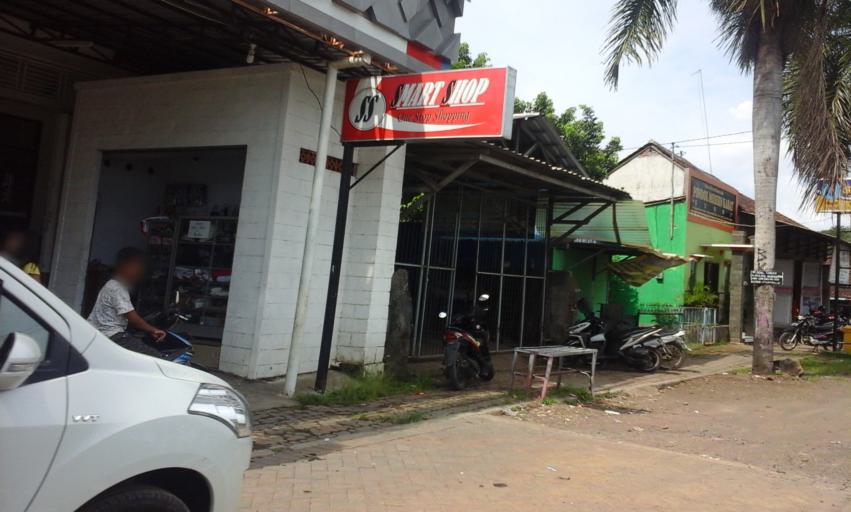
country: ID
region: East Java
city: Kertosari
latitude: -8.2625
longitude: 114.3308
